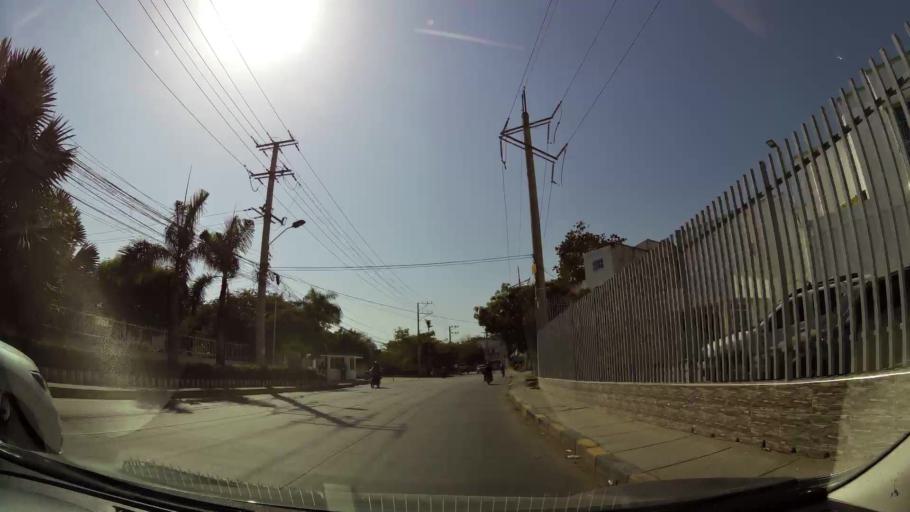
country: CO
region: Bolivar
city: Cartagena
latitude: 10.3880
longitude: -75.4677
